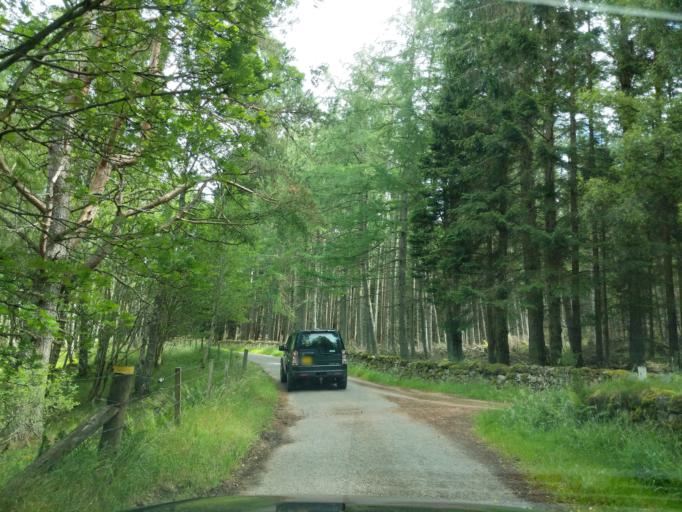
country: GB
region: Scotland
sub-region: Aberdeenshire
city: Aboyne
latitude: 57.0562
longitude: -2.7457
